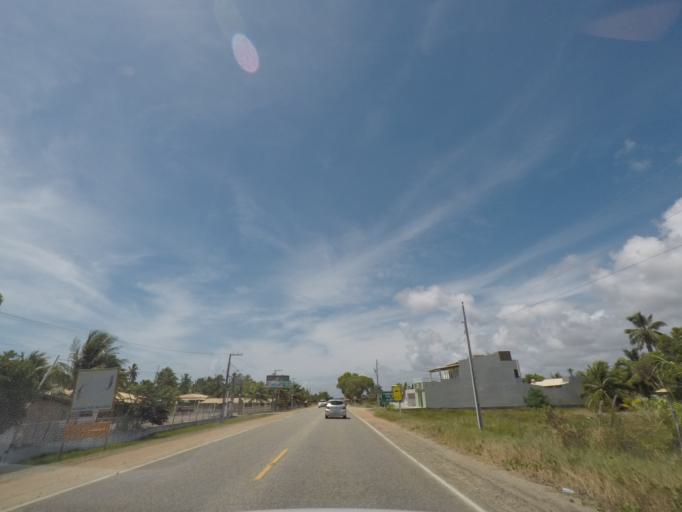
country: BR
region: Sergipe
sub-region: Sao Cristovao
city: Sao Cristovao
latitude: -11.2121
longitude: -37.2162
